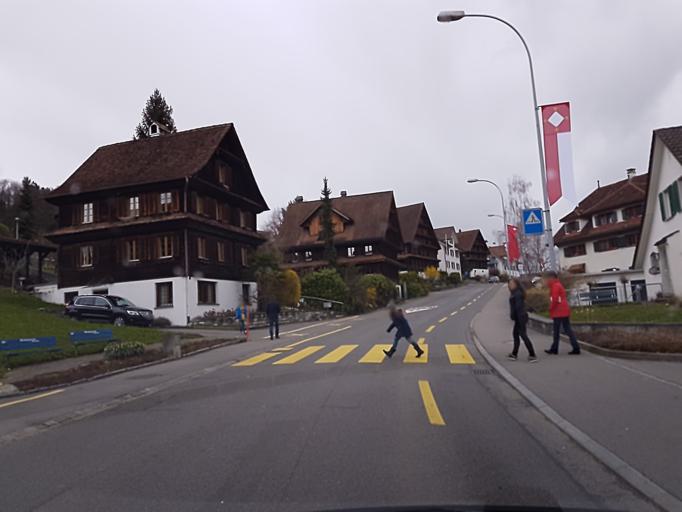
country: CH
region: Lucerne
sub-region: Lucerne-Land District
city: Udligenswil
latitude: 47.0659
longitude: 8.4083
